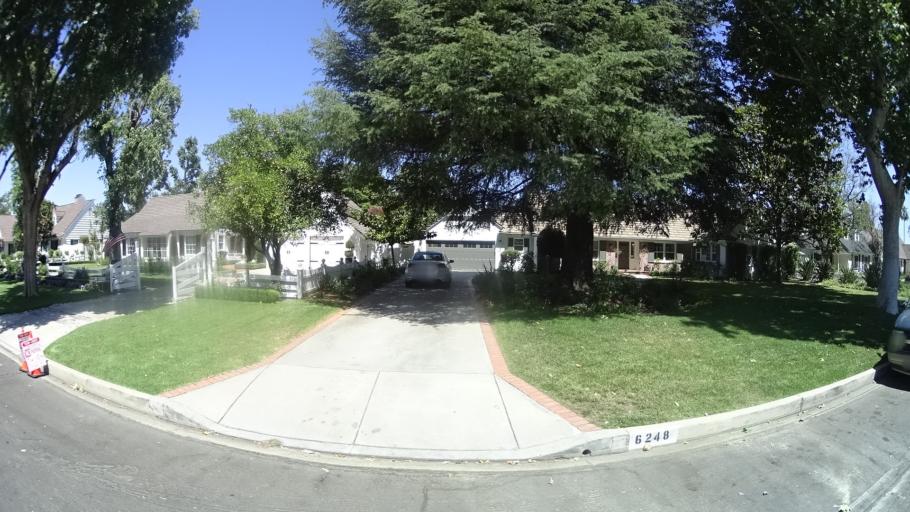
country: US
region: California
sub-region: Los Angeles County
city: Van Nuys
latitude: 34.1845
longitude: -118.4699
